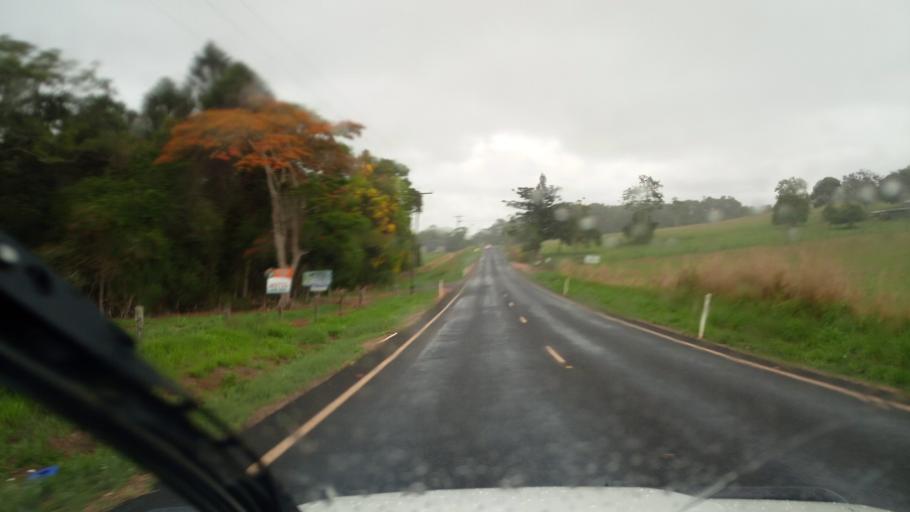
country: AU
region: Queensland
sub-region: Tablelands
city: Atherton
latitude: -17.2786
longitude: 145.5906
